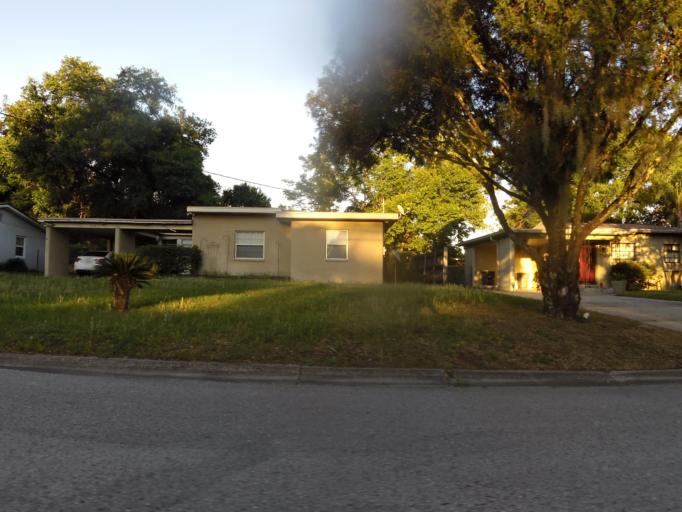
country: US
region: Florida
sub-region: Duval County
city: Jacksonville
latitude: 30.2592
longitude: -81.6395
